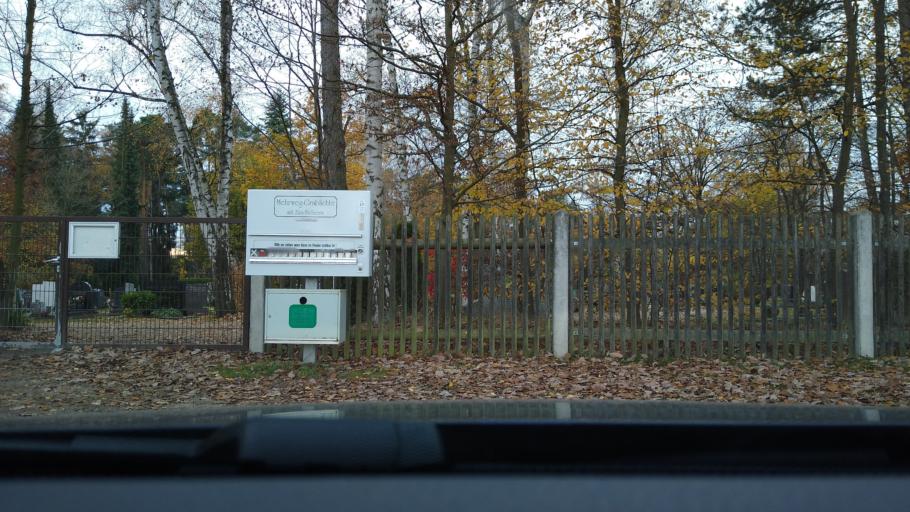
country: DE
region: Bavaria
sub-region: Regierungsbezirk Mittelfranken
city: Schwabach
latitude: 49.3377
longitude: 11.0391
